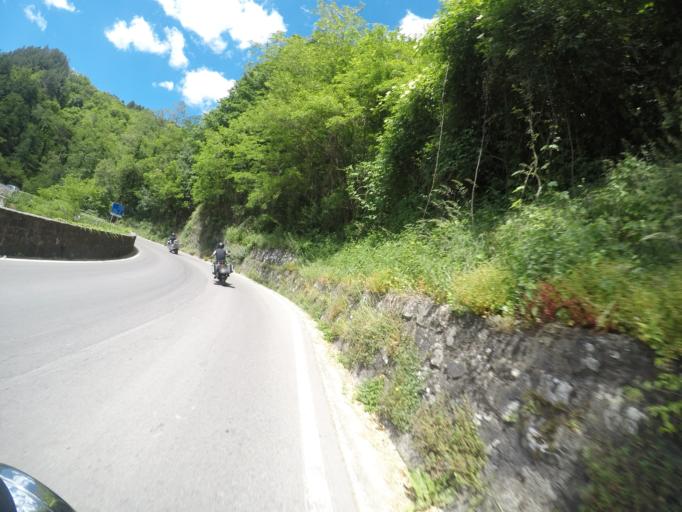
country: IT
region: Tuscany
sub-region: Provincia di Lucca
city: San Romano in Garfagnana
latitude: 44.1682
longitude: 10.3517
